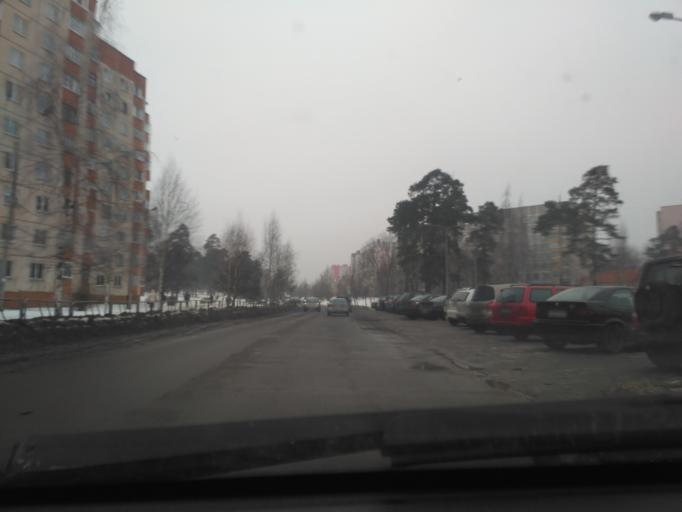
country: BY
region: Minsk
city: Horad Barysaw
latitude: 54.2217
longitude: 28.4884
